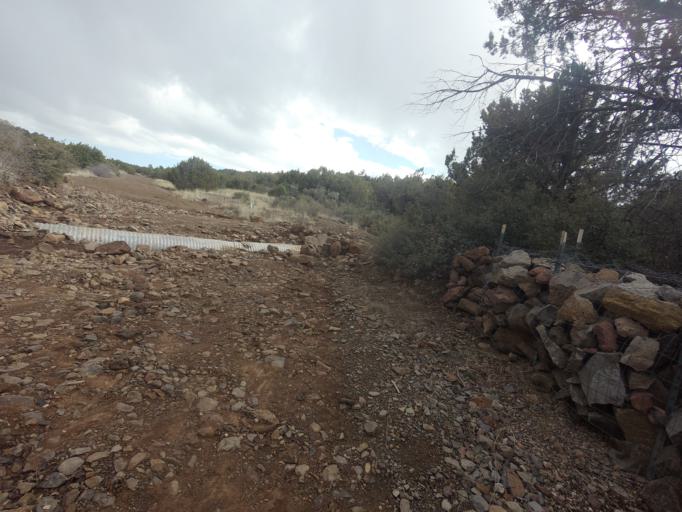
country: US
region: Arizona
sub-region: Gila County
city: Pine
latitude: 34.4062
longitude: -111.5772
